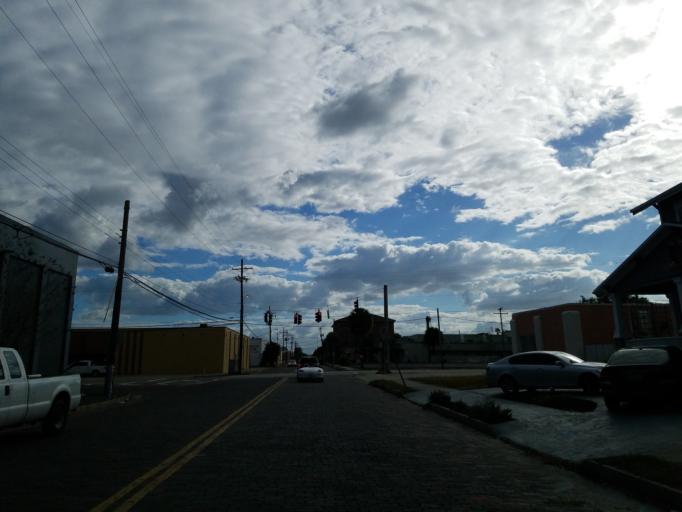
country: US
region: Florida
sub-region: Hillsborough County
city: Tampa
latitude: 27.9504
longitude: -82.4726
